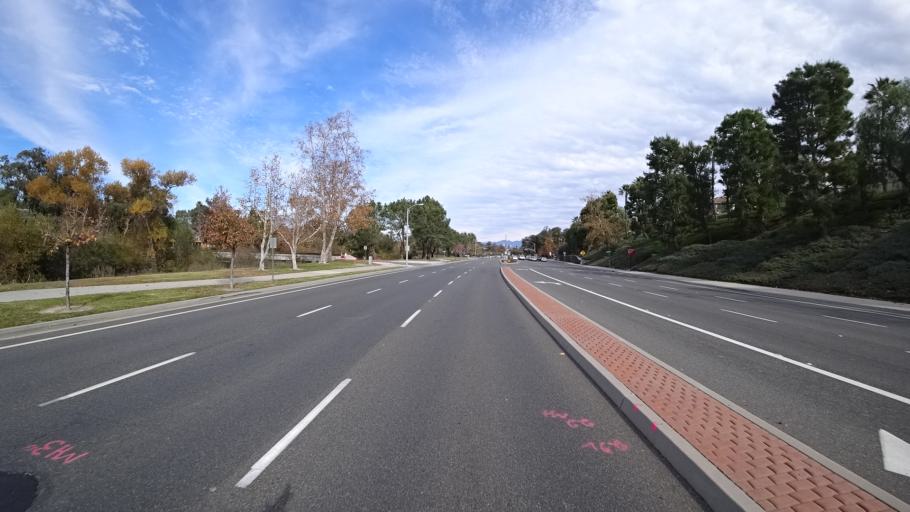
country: US
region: California
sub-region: Orange County
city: Aliso Viejo
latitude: 33.5820
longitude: -117.7080
